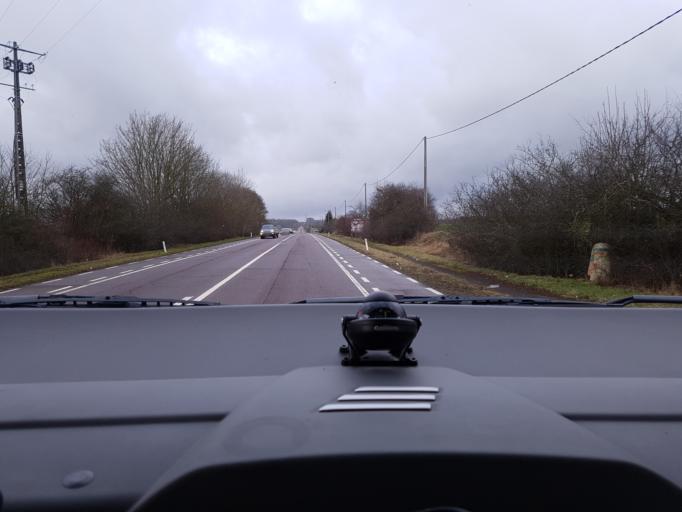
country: LU
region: Luxembourg
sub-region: Canton de Capellen
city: Steinfort
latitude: 49.6585
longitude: 5.8968
